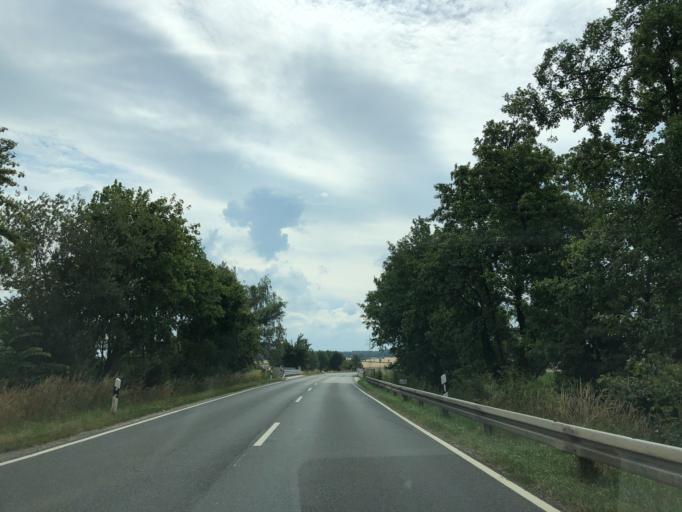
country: DE
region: Bavaria
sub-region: Regierungsbezirk Mittelfranken
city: Muhlhausen
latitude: 49.7499
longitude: 10.7720
